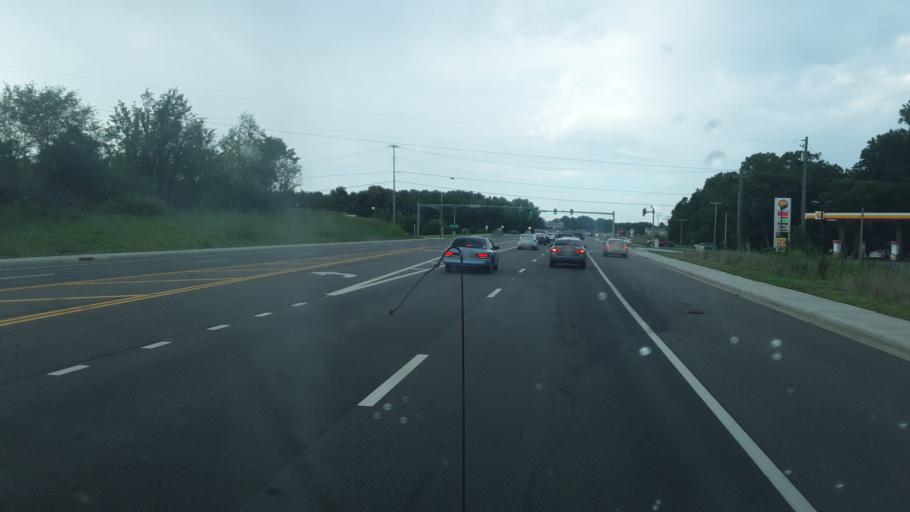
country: US
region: Tennessee
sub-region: Montgomery County
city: Clarksville
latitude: 36.5597
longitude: -87.2885
